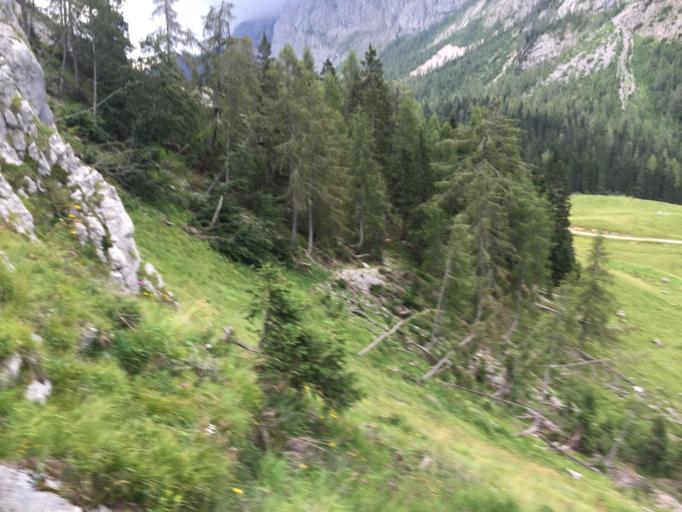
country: IT
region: Friuli Venezia Giulia
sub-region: Provincia di Udine
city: Forni Avoltri
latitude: 46.5641
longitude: 12.7645
